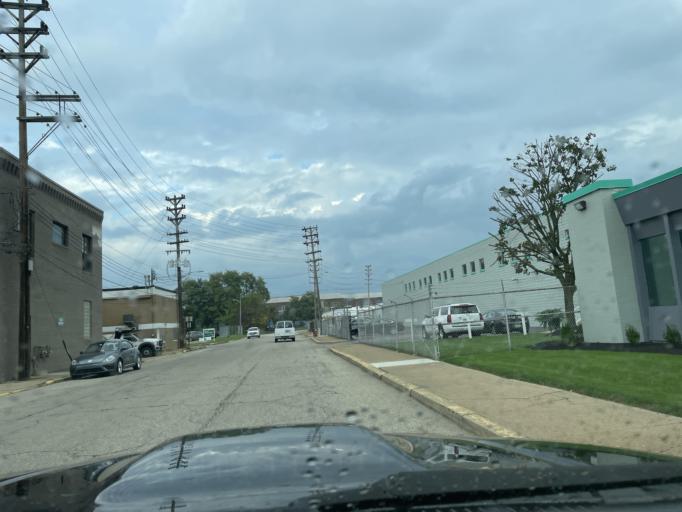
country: US
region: Pennsylvania
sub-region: Westmoreland County
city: New Kensington
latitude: 40.5686
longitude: -79.7698
